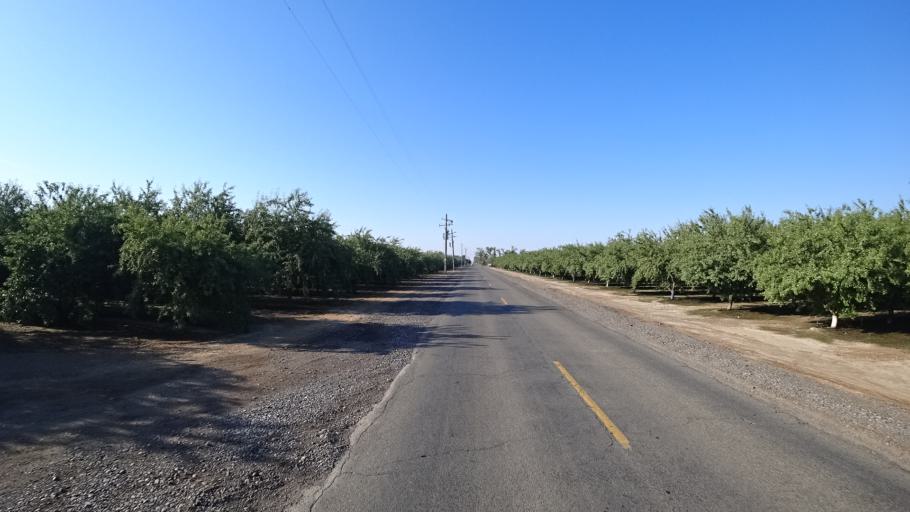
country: US
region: California
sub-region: Kings County
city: Lemoore
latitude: 36.2891
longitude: -119.7447
